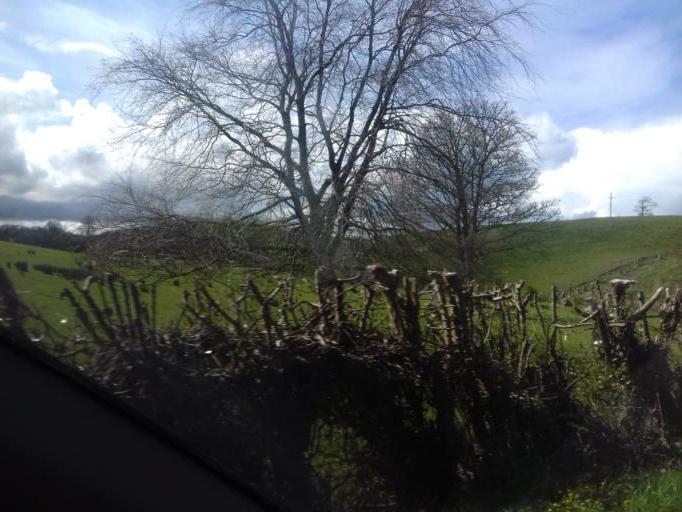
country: GB
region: Northern Ireland
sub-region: Fermanagh District
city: Enniskillen
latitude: 54.3858
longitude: -7.6963
